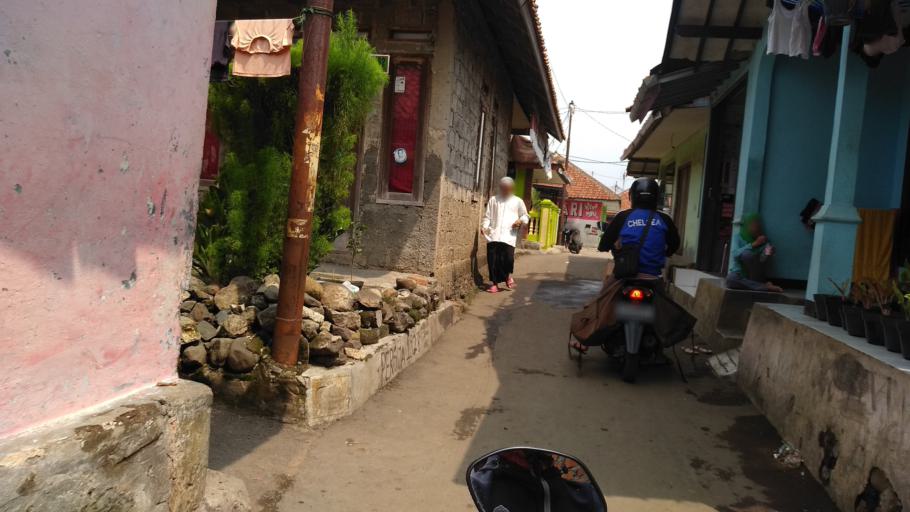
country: ID
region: West Java
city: Ciampea
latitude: -6.5605
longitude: 106.7456
